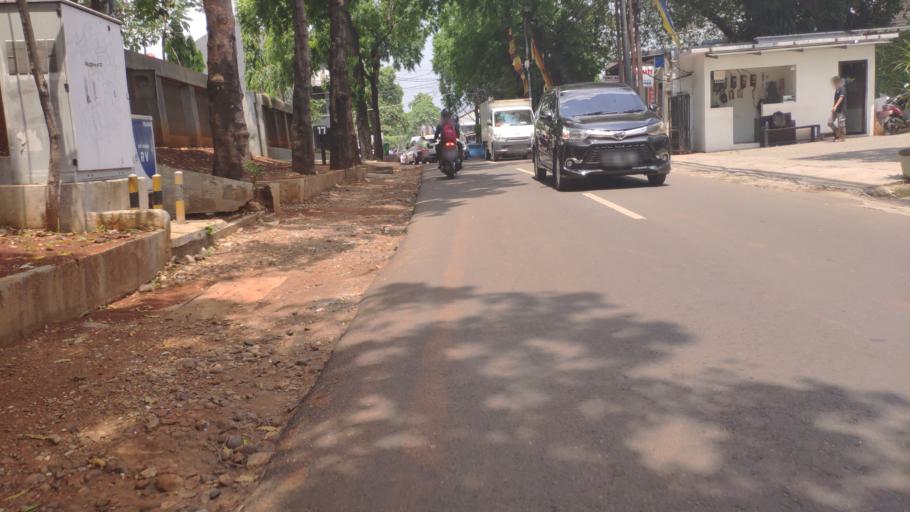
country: ID
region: Jakarta Raya
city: Jakarta
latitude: -6.2696
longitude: 106.8239
